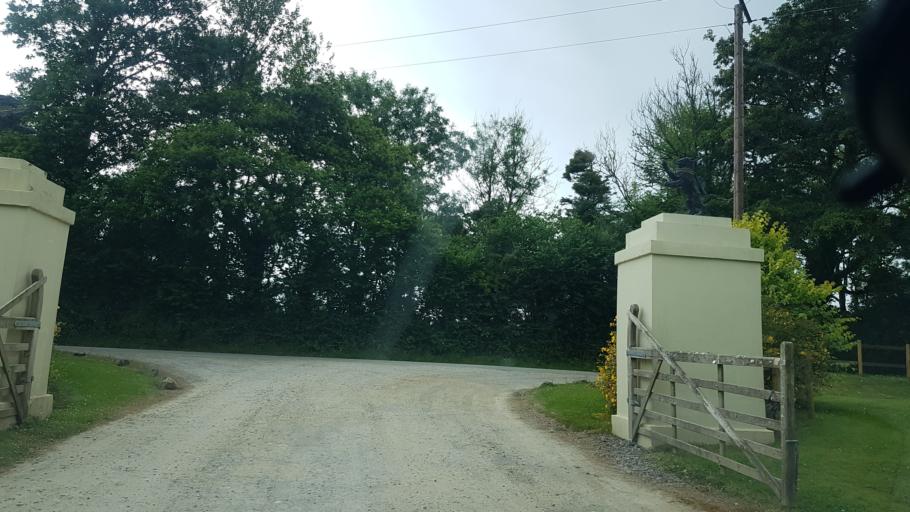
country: GB
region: Wales
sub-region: Pembrokeshire
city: Llangwm
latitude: 51.7846
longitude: -4.8894
